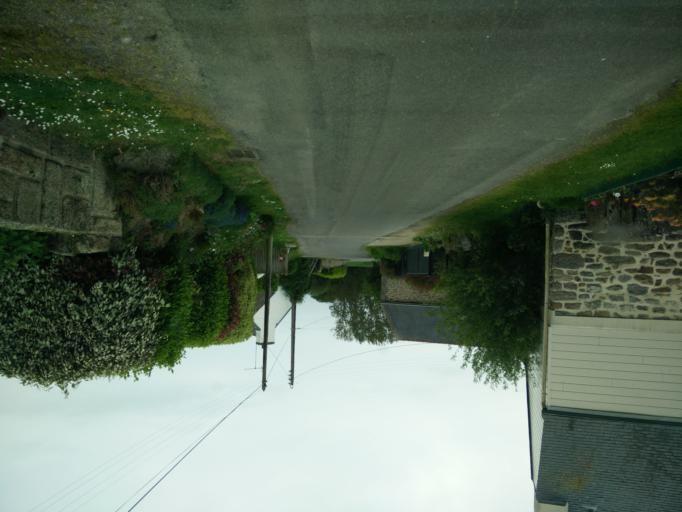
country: FR
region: Brittany
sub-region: Departement du Finistere
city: Tregunc
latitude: 47.8304
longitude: -3.8769
